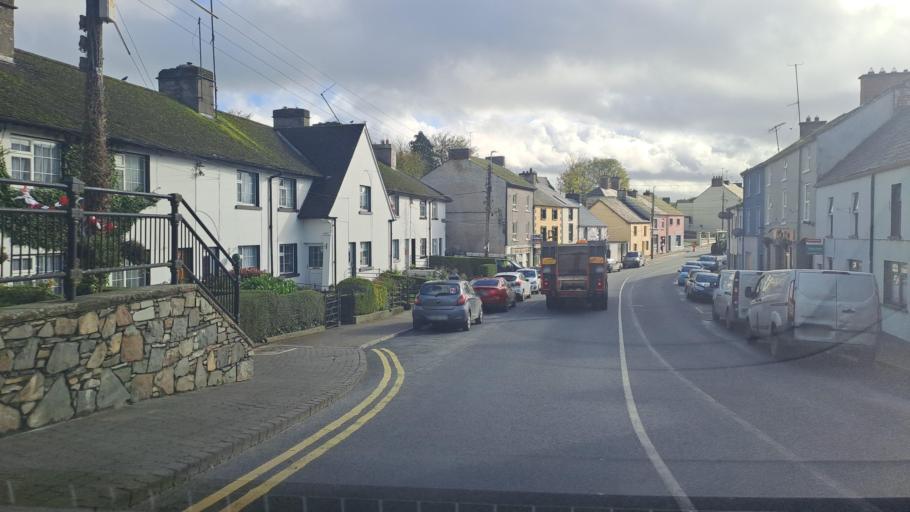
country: IE
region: Ulster
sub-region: County Monaghan
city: Monaghan
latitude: 54.1273
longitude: -6.9018
